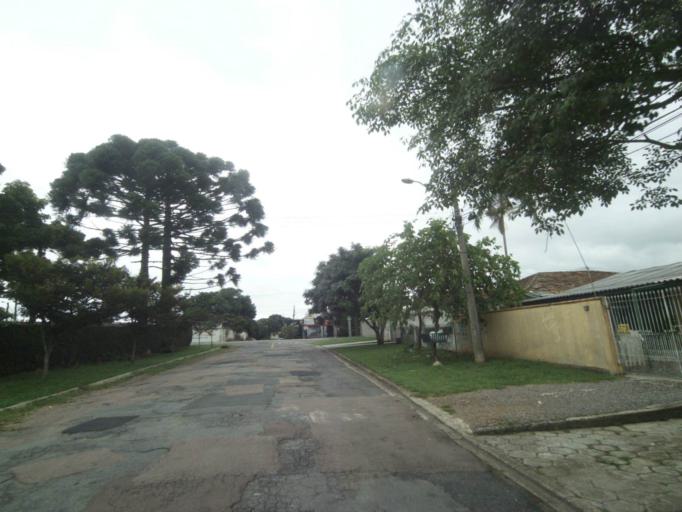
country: BR
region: Parana
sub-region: Curitiba
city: Curitiba
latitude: -25.4876
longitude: -49.2824
